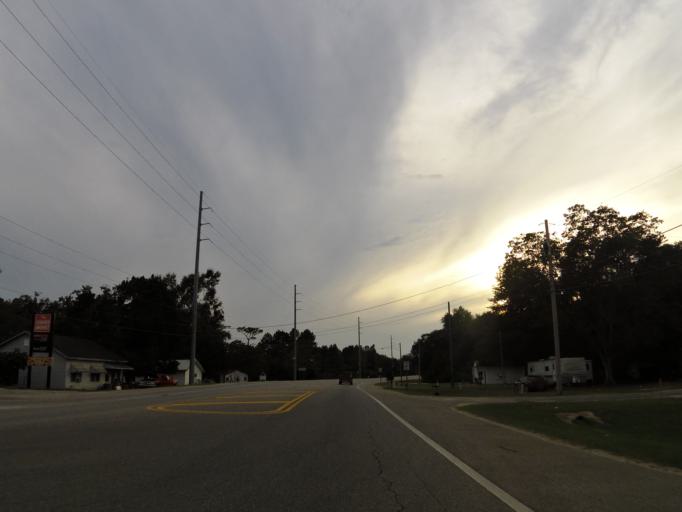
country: US
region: Alabama
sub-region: Baldwin County
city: Bay Minette
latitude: 30.8908
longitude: -87.7527
